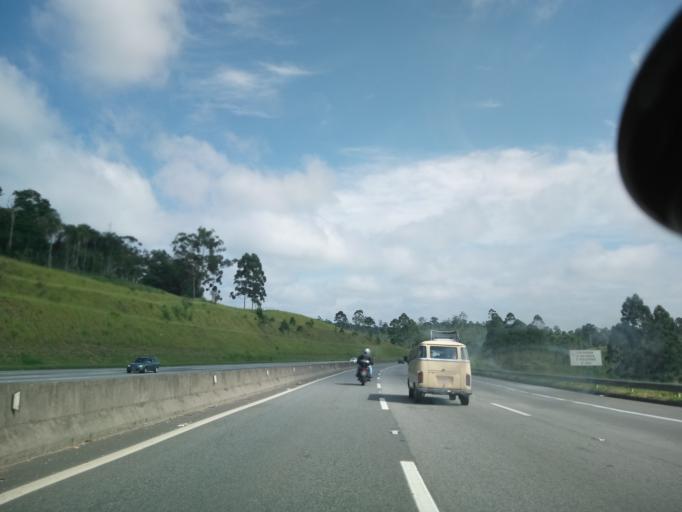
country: BR
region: Sao Paulo
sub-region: Itapecerica Da Serra
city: Itapecerica da Serra
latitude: -23.7437
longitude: -46.8125
